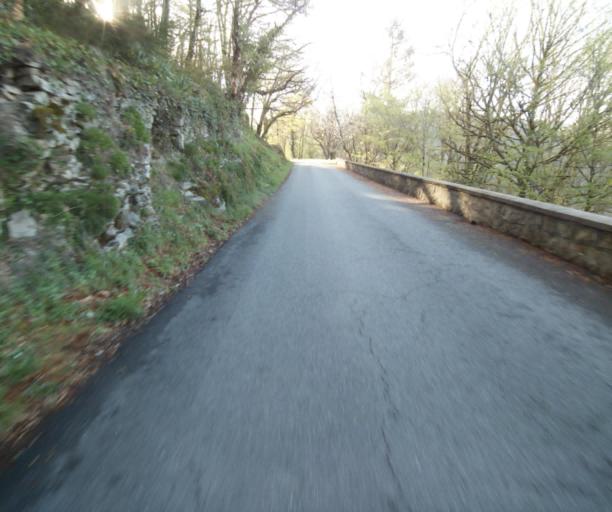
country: FR
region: Limousin
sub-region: Departement de la Correze
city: Correze
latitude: 45.3006
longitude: 1.8445
